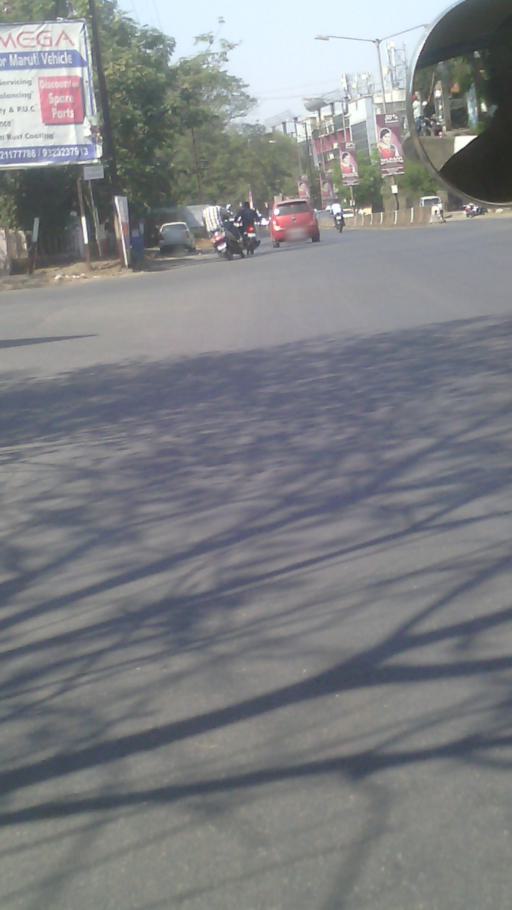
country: IN
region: Maharashtra
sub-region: Thane
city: Dombivli
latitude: 19.2098
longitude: 73.1106
